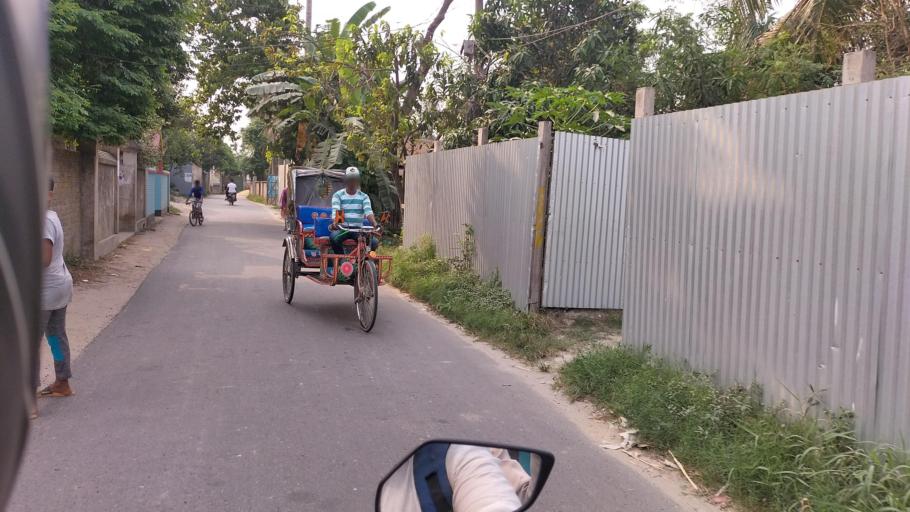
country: BD
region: Dhaka
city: Azimpur
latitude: 23.6672
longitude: 90.3486
